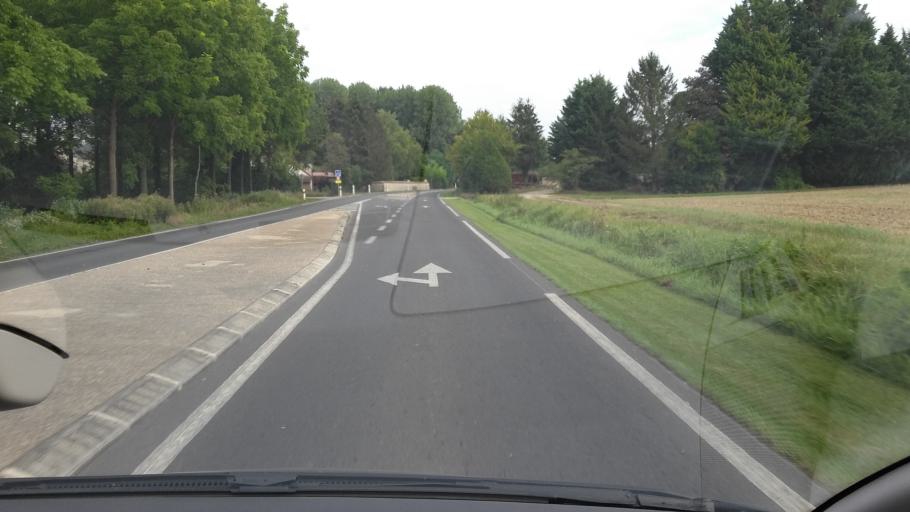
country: FR
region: Champagne-Ardenne
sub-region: Departement de la Marne
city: Mareuil-sur-Ay
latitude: 49.0801
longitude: 4.0697
